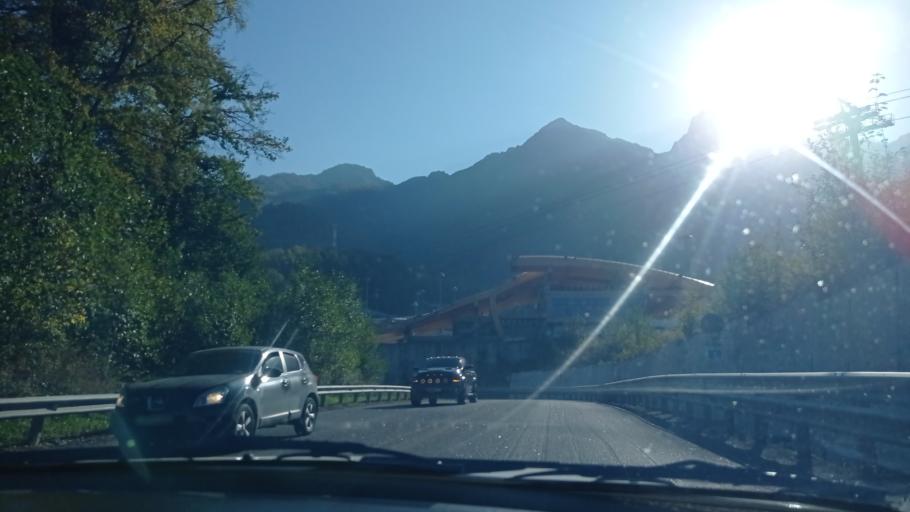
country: RU
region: Krasnodarskiy
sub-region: Sochi City
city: Krasnaya Polyana
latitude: 43.6690
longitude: 40.2896
